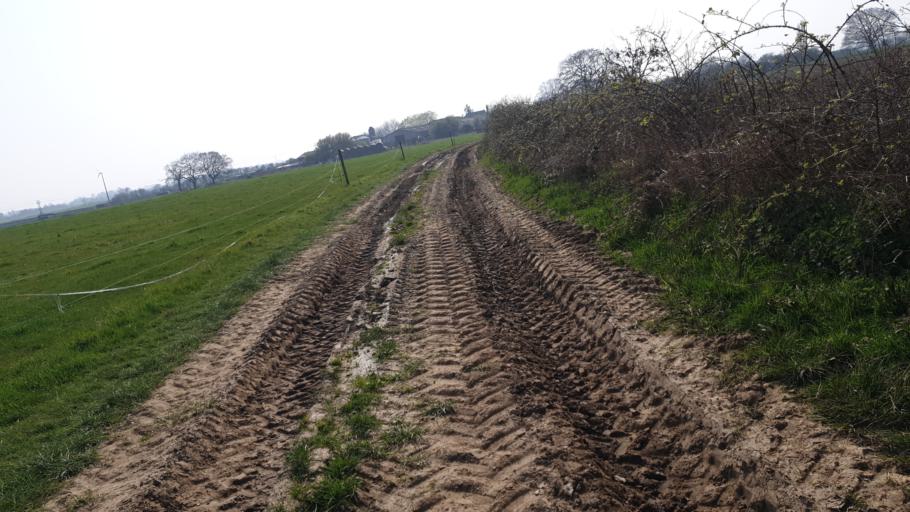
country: GB
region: England
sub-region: Essex
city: Mistley
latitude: 51.9249
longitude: 1.1595
